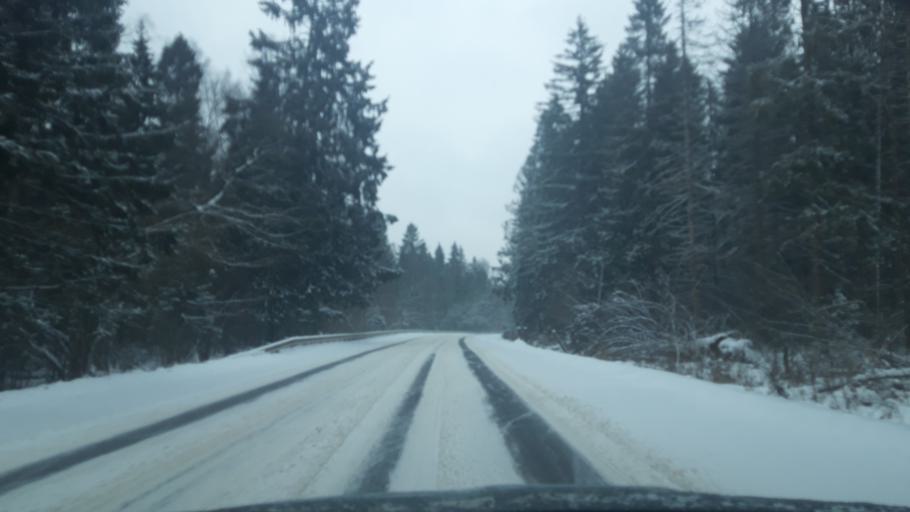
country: RU
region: Moskovskaya
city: Avtopoligon
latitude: 56.2857
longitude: 37.3805
